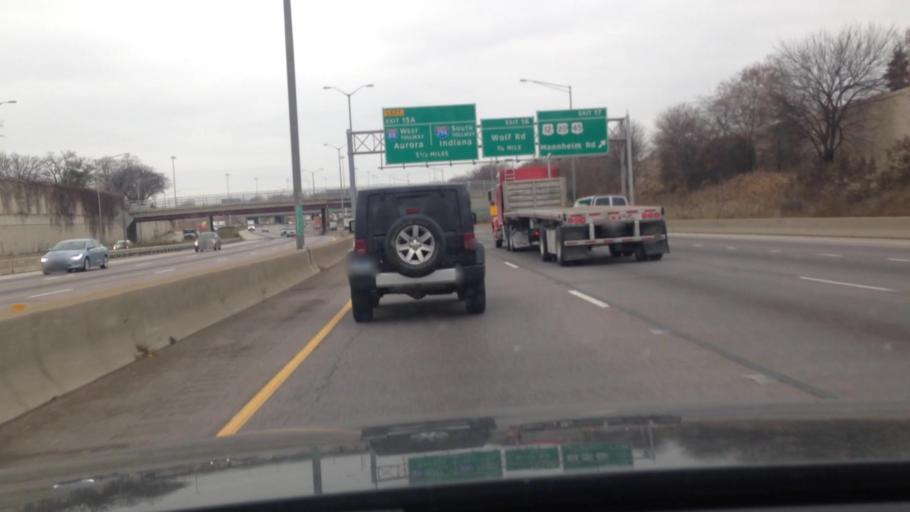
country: US
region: Illinois
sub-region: Cook County
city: Bellwood
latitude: 41.8708
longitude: -87.8755
